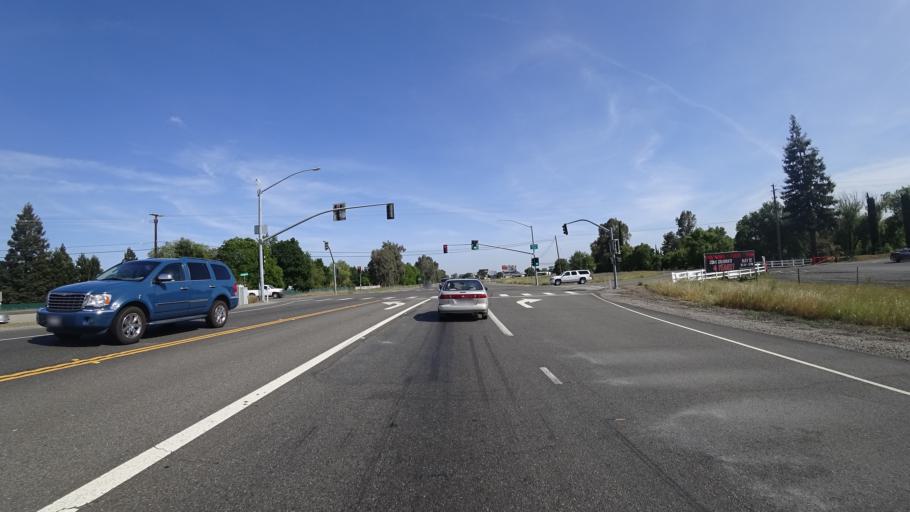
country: US
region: California
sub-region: Butte County
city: Chico
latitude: 39.7906
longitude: -121.8918
